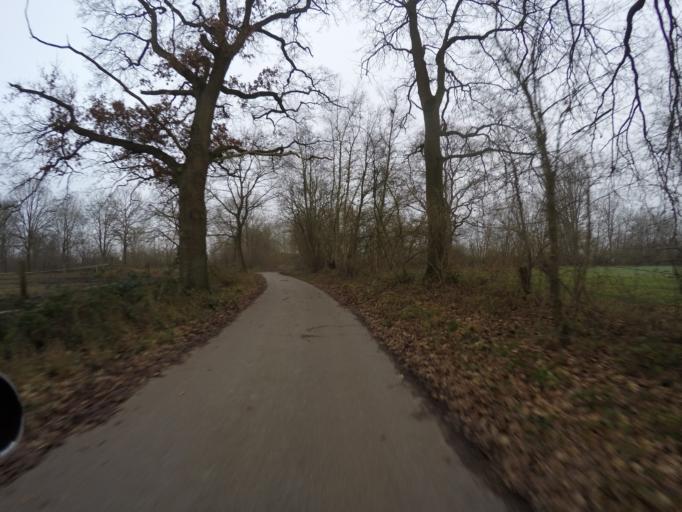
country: DE
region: Schleswig-Holstein
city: Tangstedt
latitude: 53.6782
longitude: 9.8400
